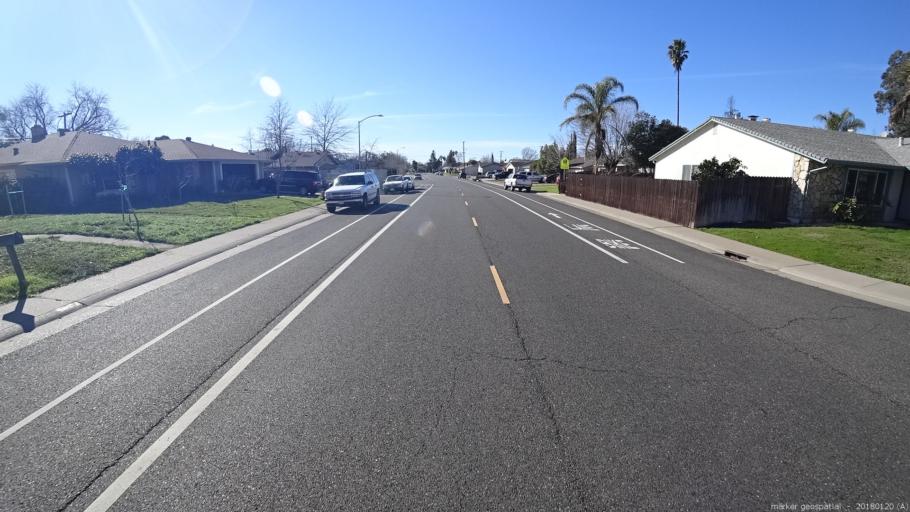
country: US
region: California
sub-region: Sacramento County
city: Rancho Cordova
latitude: 38.5682
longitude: -121.3225
